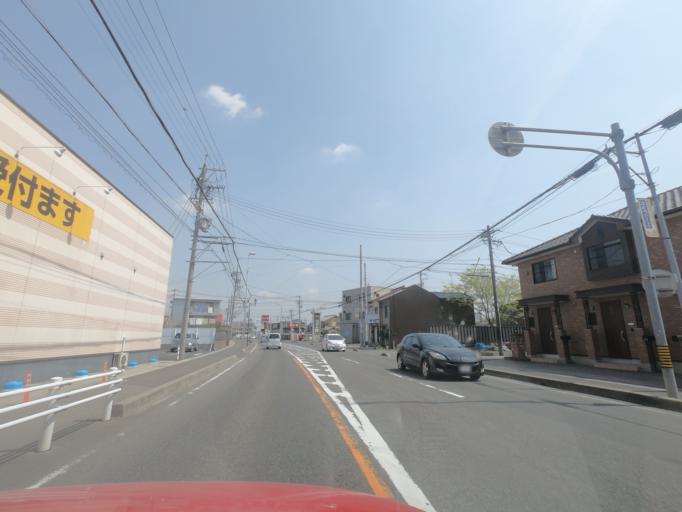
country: JP
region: Aichi
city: Kasugai
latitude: 35.2574
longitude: 136.9935
